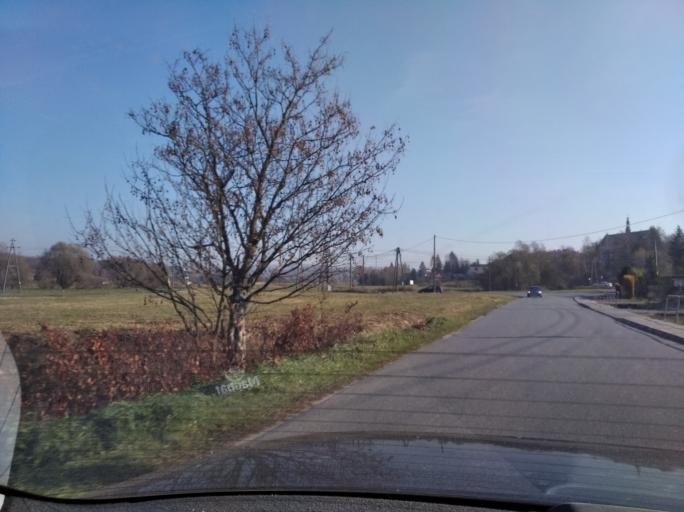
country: PL
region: Subcarpathian Voivodeship
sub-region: Powiat ropczycko-sedziszowski
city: Wielopole Skrzynskie
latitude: 49.9463
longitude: 21.6082
